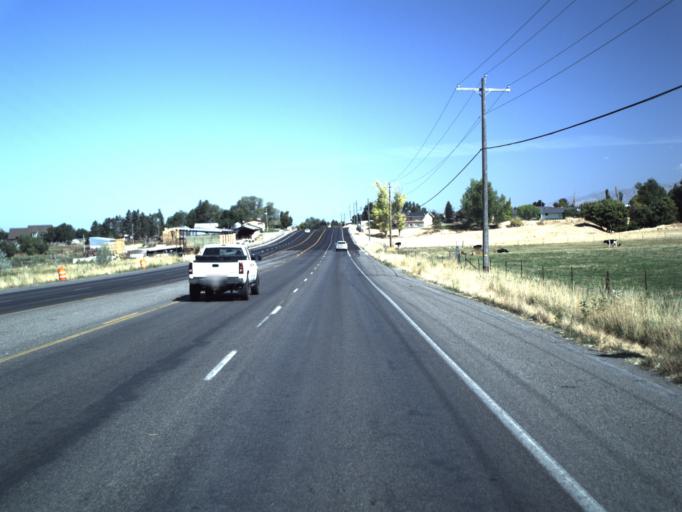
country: US
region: Utah
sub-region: Cache County
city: Nibley
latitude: 41.6533
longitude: -111.8327
